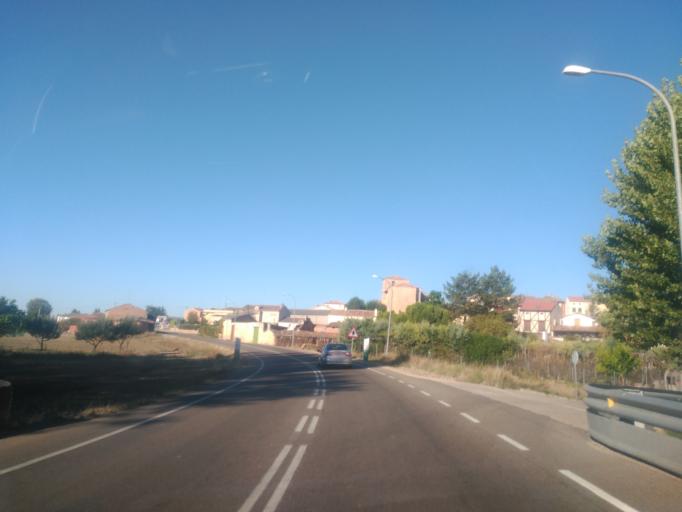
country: ES
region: Castille and Leon
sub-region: Provincia de Burgos
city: Quemada
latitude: 41.6999
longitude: -3.5718
